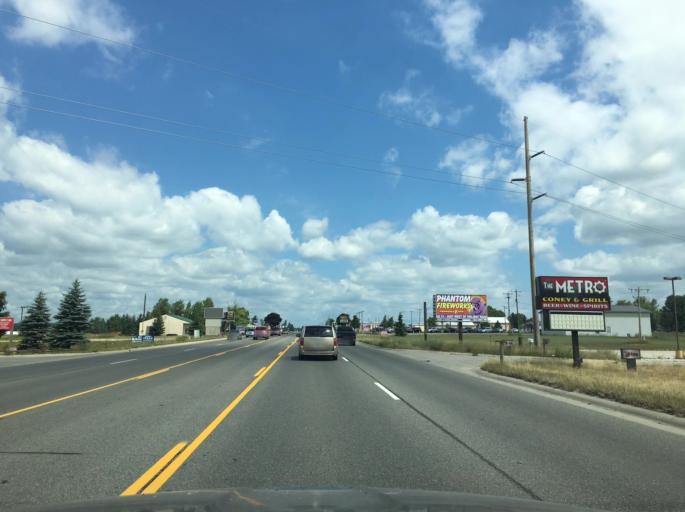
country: US
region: Michigan
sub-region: Grand Traverse County
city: Traverse City
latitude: 44.6784
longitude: -85.6563
